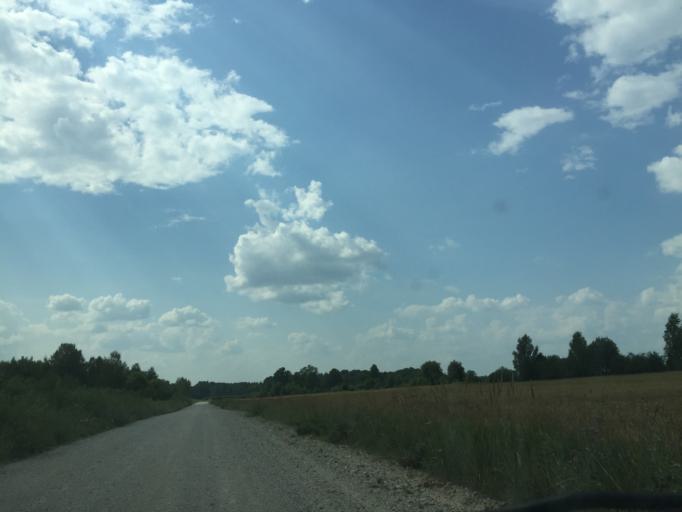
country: LV
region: Auces Novads
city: Auce
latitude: 56.4114
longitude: 23.0247
